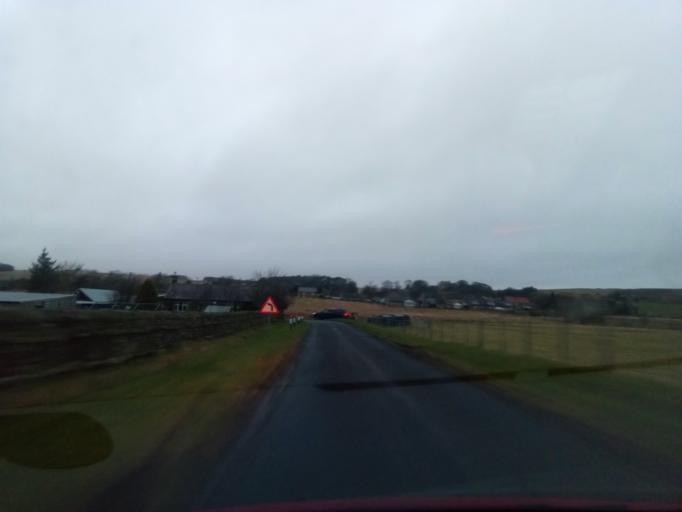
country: GB
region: England
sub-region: Northumberland
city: Otterburn
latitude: 55.2289
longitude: -2.1002
